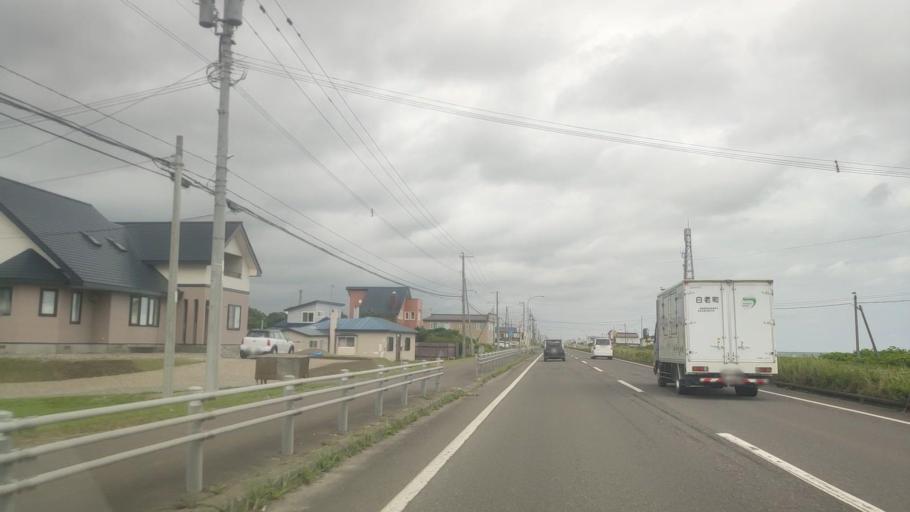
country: JP
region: Hokkaido
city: Shiraoi
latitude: 42.4676
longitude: 141.2261
